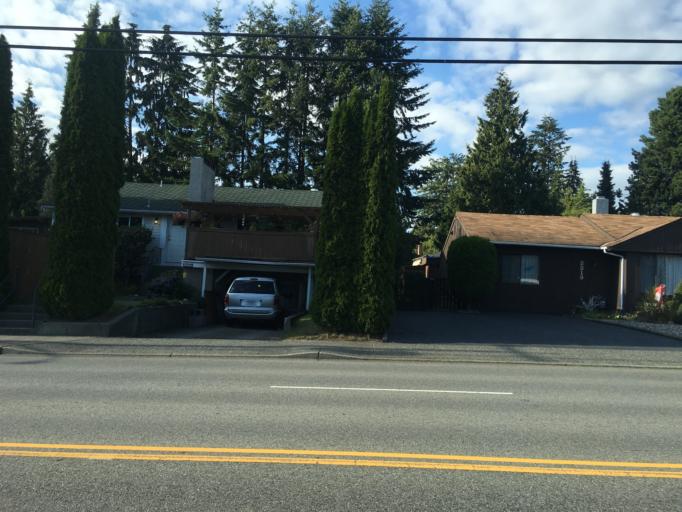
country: CA
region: British Columbia
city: Port Moody
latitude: 49.2490
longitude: -122.8334
